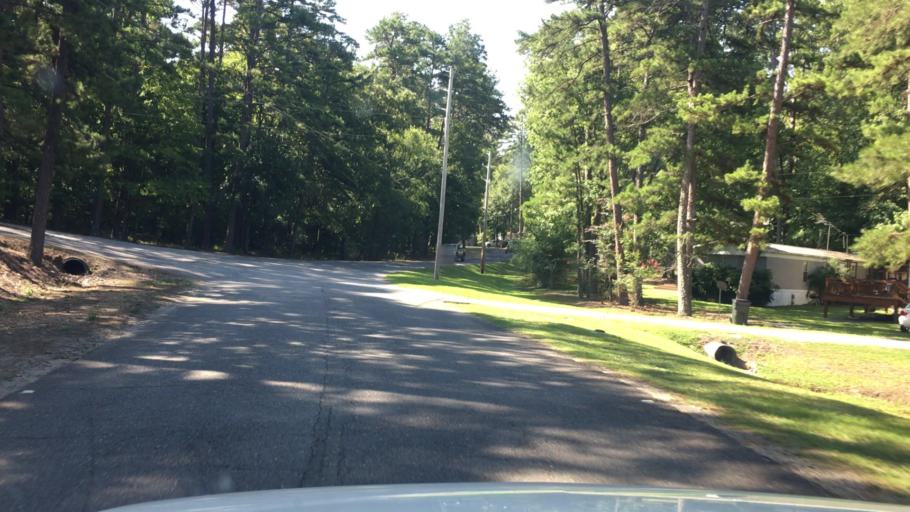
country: US
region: Arkansas
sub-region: Garland County
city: Piney
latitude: 34.5459
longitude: -93.3613
